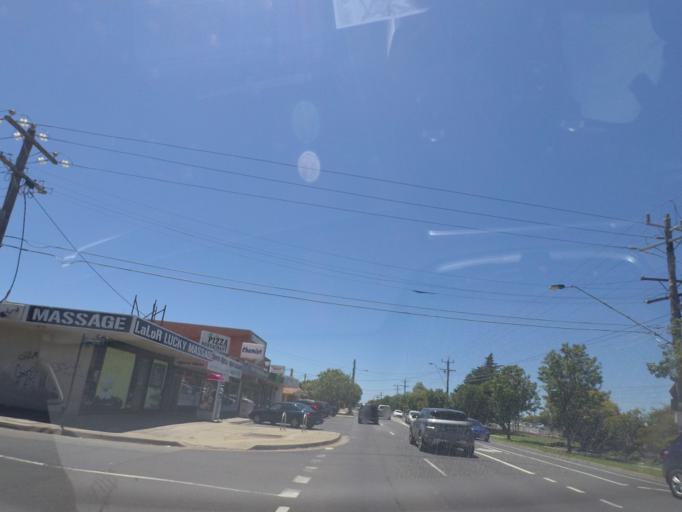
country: AU
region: Victoria
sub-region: Whittlesea
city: Lalor
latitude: -37.6721
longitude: 145.0153
